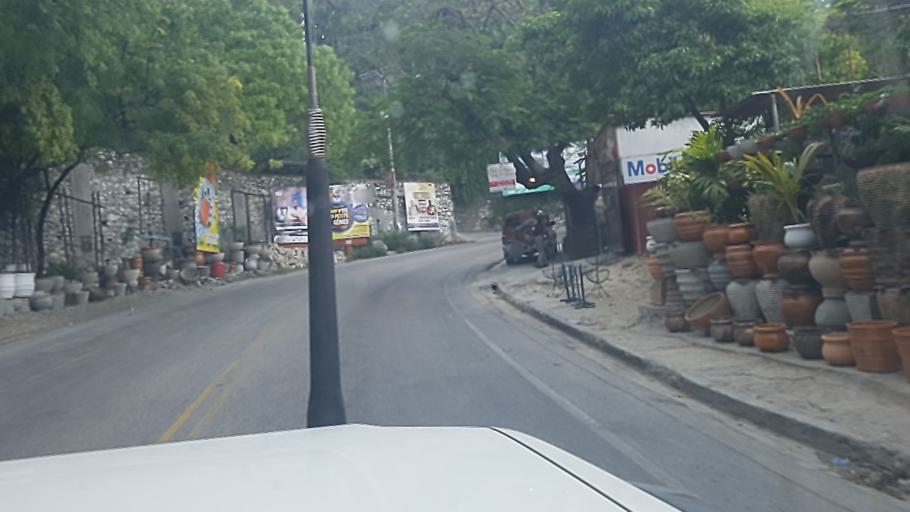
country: HT
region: Ouest
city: Delmas 73
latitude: 18.5295
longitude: -72.3002
